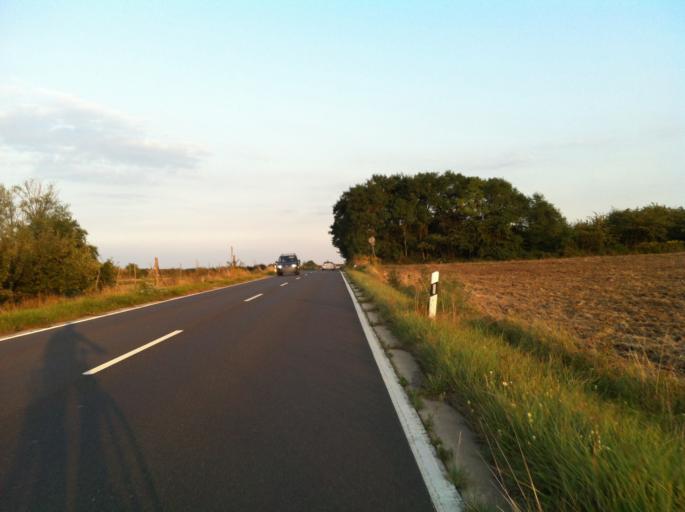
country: DE
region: Rheinland-Pfalz
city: Wackernheim
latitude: 49.9766
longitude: 8.1017
